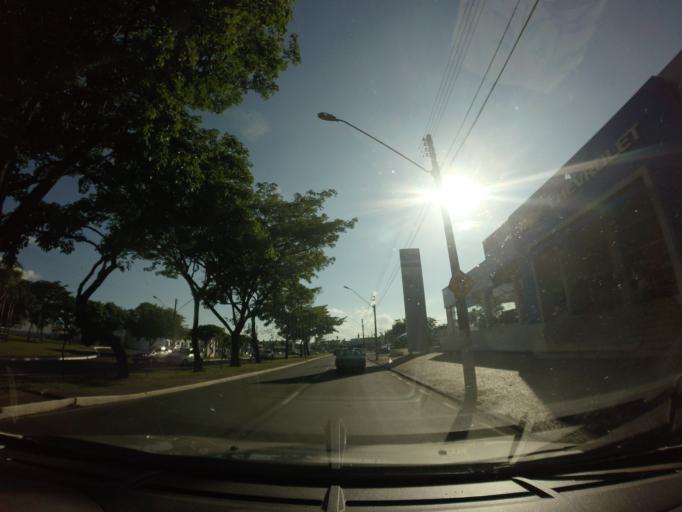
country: BR
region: Sao Paulo
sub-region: Rio Claro
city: Rio Claro
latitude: -22.4167
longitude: -47.5743
